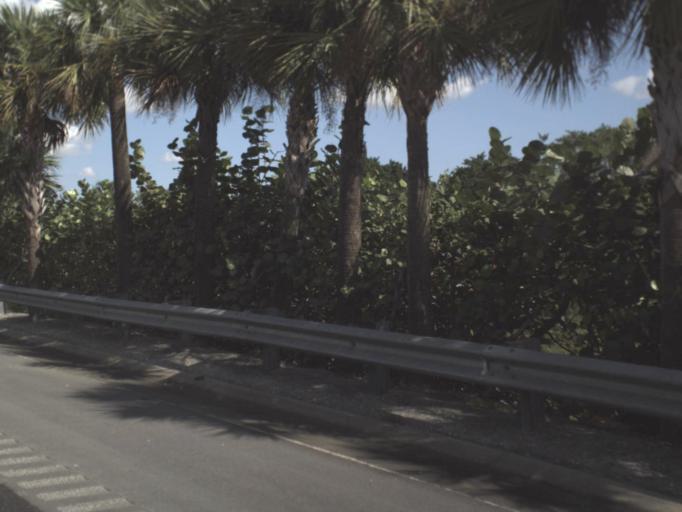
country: US
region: Florida
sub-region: Palm Beach County
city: Kings Point
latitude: 26.4066
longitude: -80.1712
